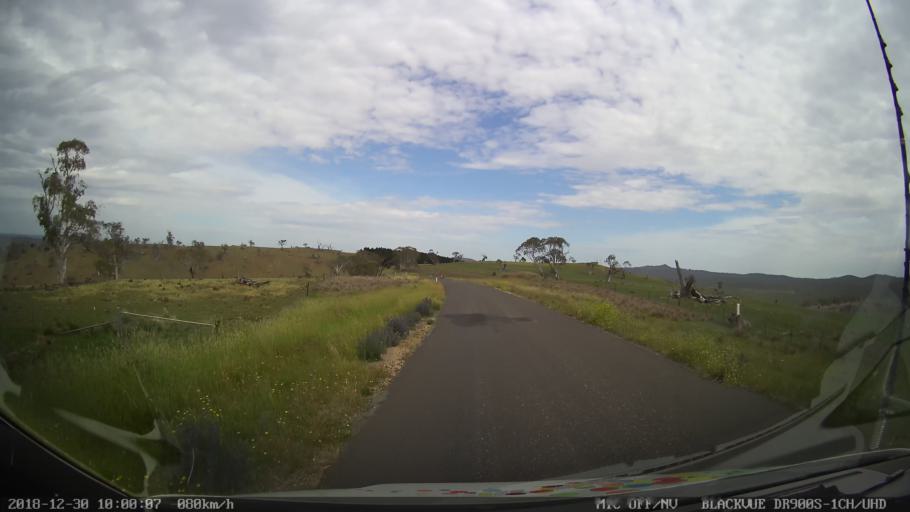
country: AU
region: New South Wales
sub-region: Cooma-Monaro
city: Cooma
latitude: -36.5185
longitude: 149.2019
